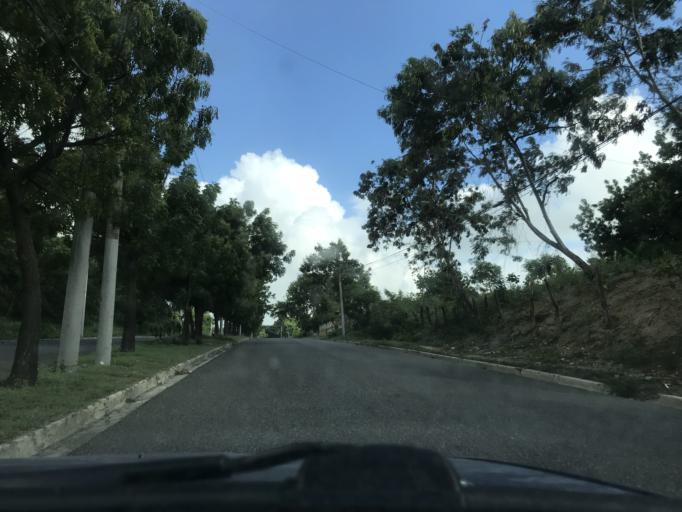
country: DO
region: Santiago
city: Santiago de los Caballeros
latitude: 19.4164
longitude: -70.7313
